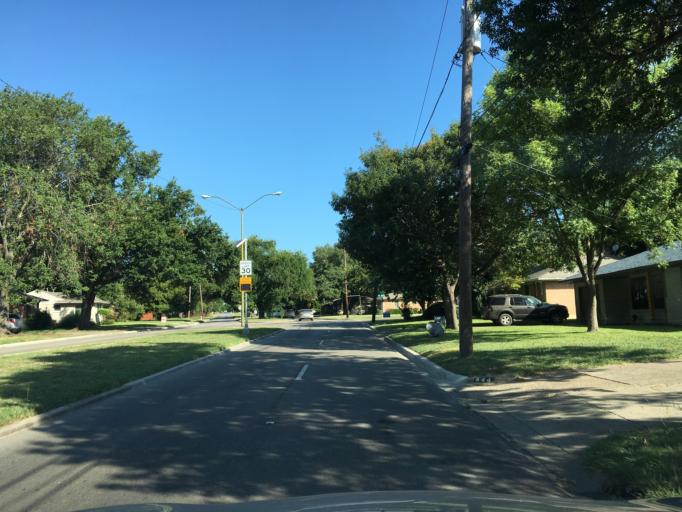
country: US
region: Texas
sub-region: Dallas County
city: Garland
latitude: 32.8580
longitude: -96.7052
